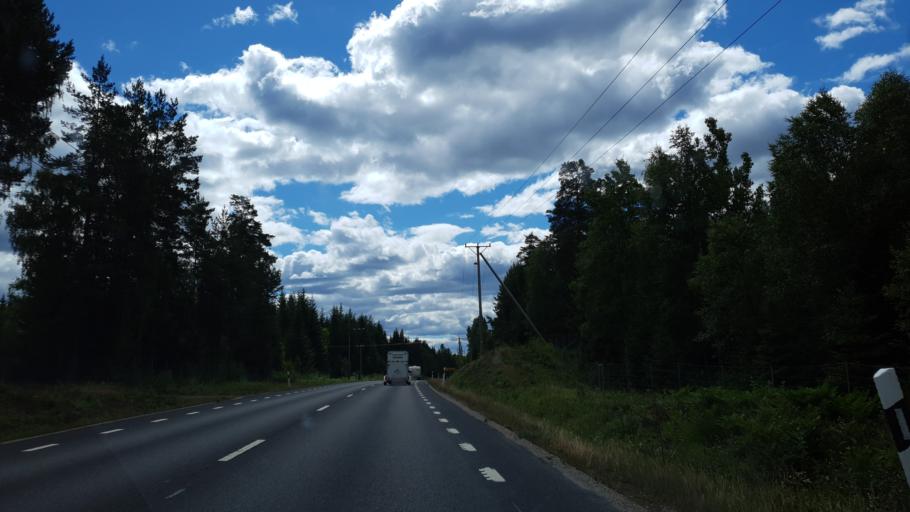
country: SE
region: Kronoberg
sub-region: Vaxjo Kommun
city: Braas
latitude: 57.2132
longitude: 15.1502
